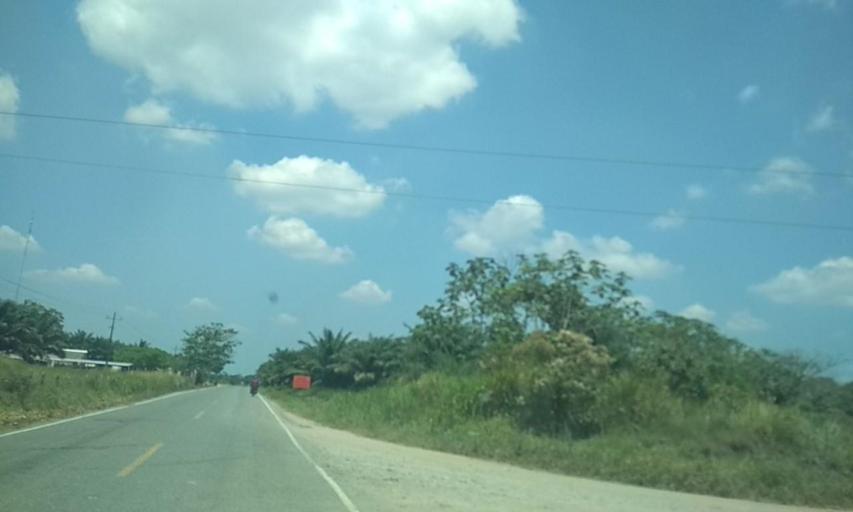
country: MX
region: Tabasco
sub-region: Huimanguillo
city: Paso de la Mina 2da. Seccion (Barrial)
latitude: 17.7543
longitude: -93.6629
